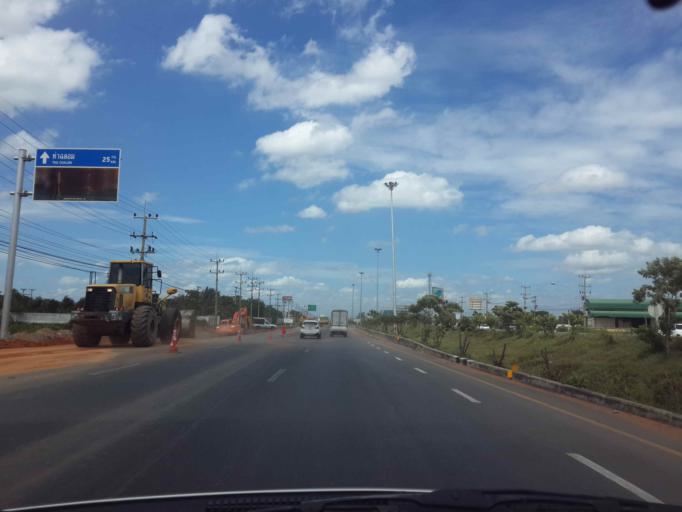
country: TH
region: Samut Songkhram
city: Samut Songkhram
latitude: 13.4507
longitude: 100.0810
